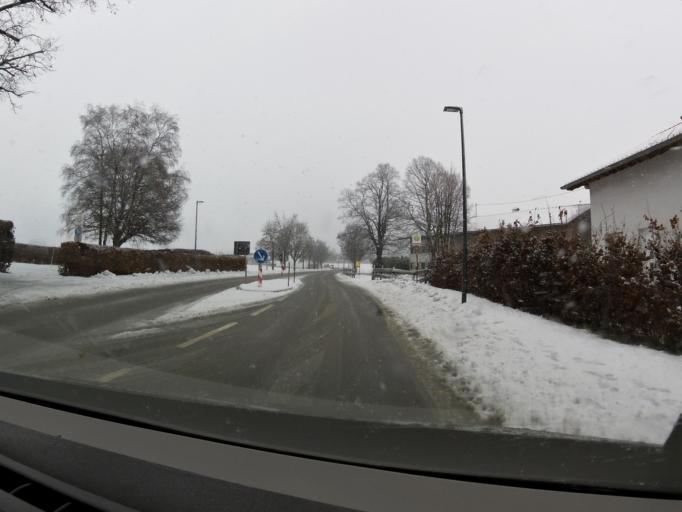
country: DE
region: Bavaria
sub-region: Upper Bavaria
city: Waakirchen
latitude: 47.7701
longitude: 11.6764
